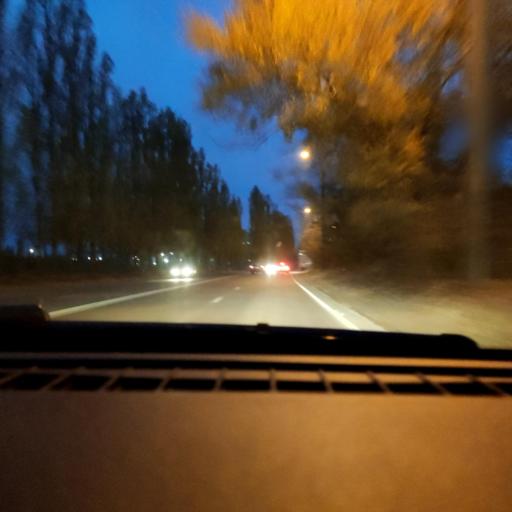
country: RU
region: Voronezj
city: Maslovka
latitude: 51.6186
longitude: 39.2588
